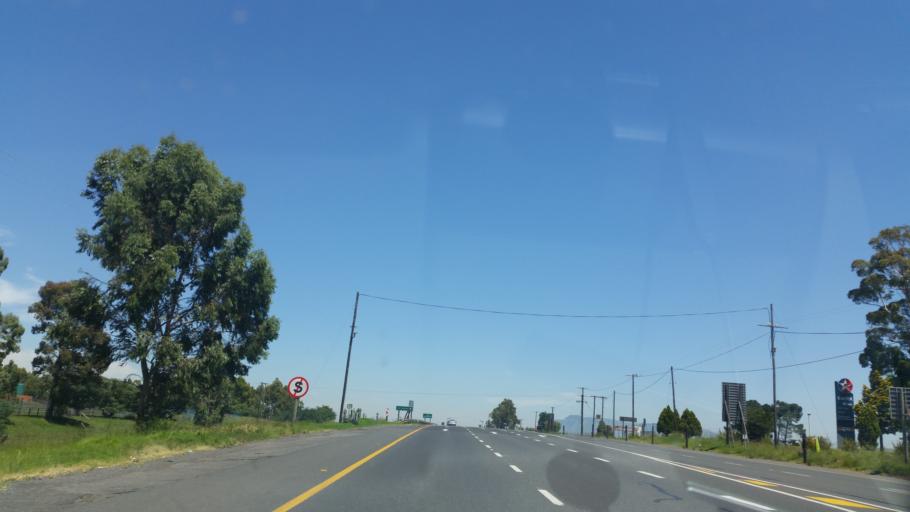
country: ZA
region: Orange Free State
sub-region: Thabo Mofutsanyana District Municipality
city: Harrismith
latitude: -28.3721
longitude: 29.3737
